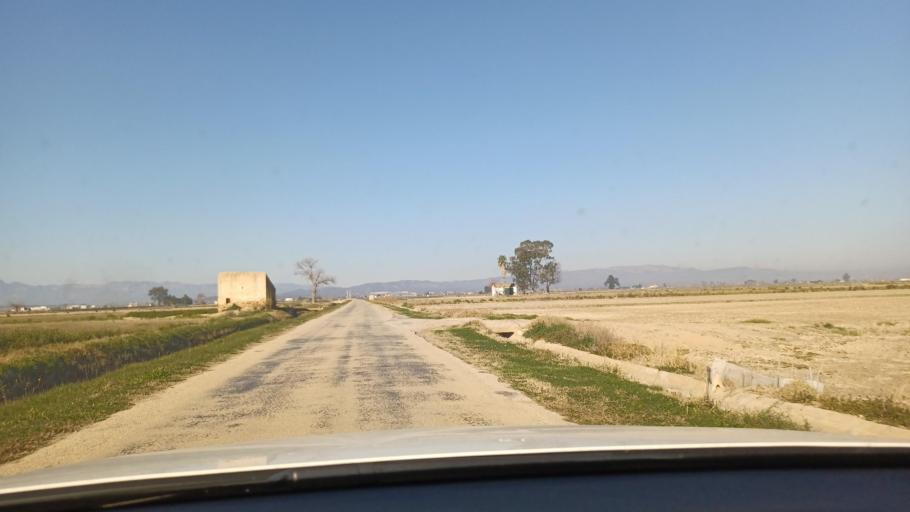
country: ES
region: Catalonia
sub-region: Provincia de Tarragona
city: Deltebre
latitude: 40.6852
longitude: 0.6547
